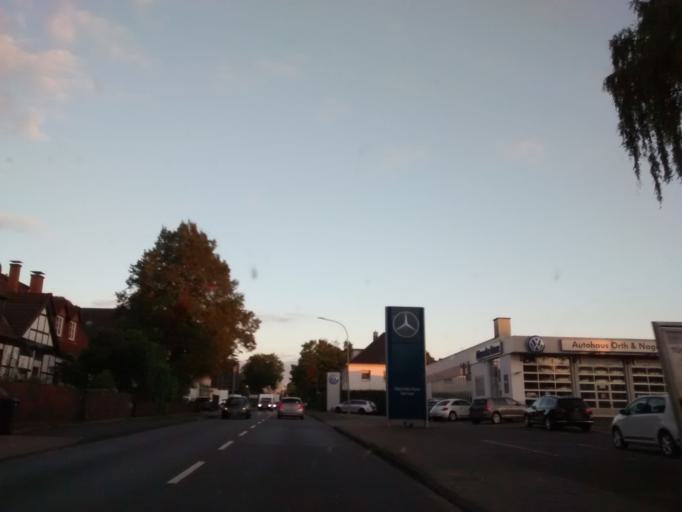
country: DE
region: North Rhine-Westphalia
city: Halle
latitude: 52.0591
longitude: 8.3655
